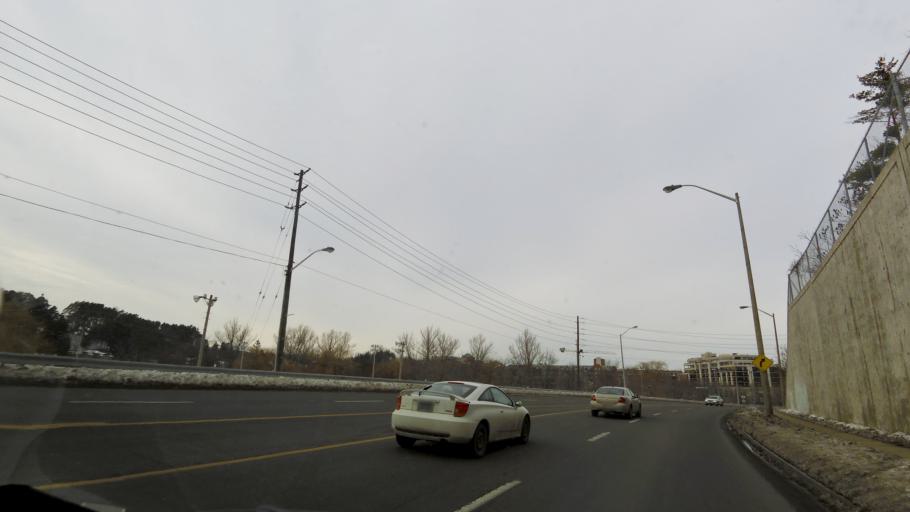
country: CA
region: Ontario
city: Vaughan
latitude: 43.7820
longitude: -79.5900
